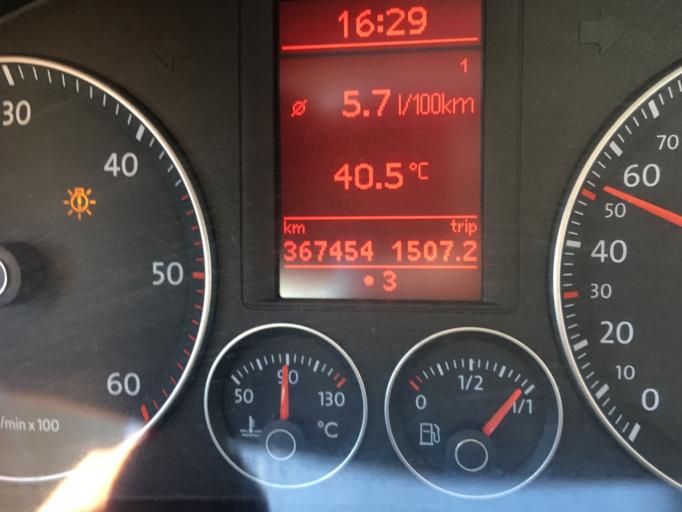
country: AL
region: Shkoder
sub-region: Rrethi i Shkodres
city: Dajc
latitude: 42.0132
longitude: 19.4061
